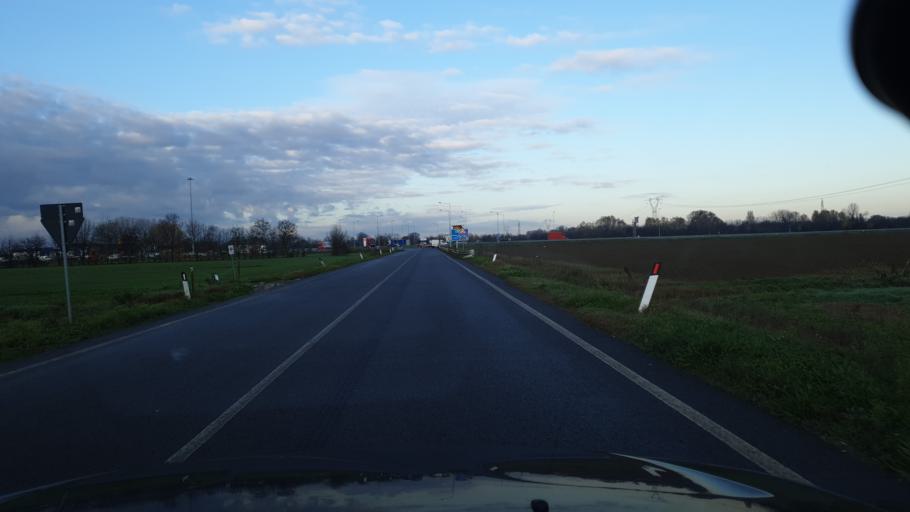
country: IT
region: Emilia-Romagna
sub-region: Provincia di Bologna
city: Calcara
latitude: 44.5305
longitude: 11.1499
